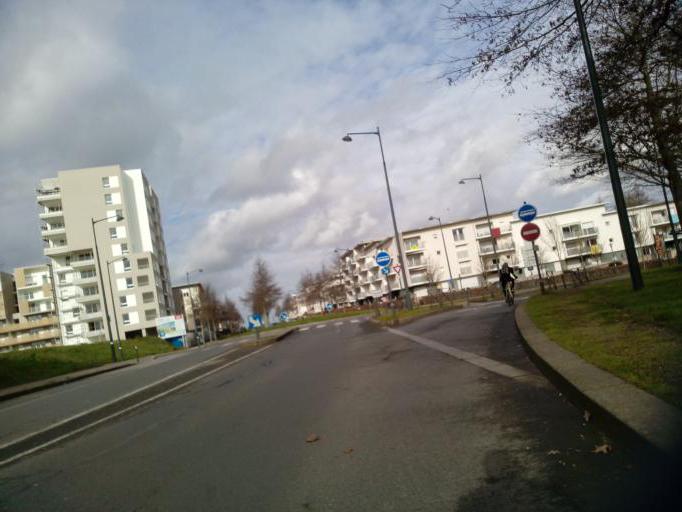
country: FR
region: Brittany
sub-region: Departement d'Ille-et-Vilaine
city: Saint-Gregoire
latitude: 48.1275
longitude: -1.7033
